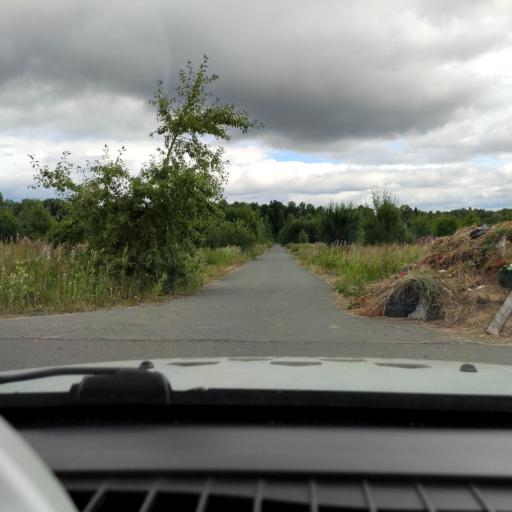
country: RU
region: Perm
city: Kondratovo
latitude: 58.0673
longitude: 56.1540
